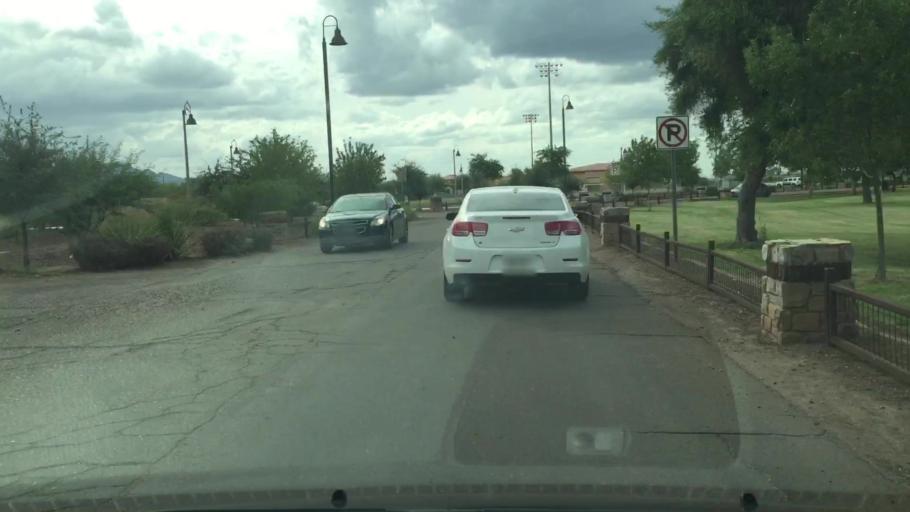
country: US
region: Arizona
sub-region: Maricopa County
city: Laveen
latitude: 33.3708
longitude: -112.1404
